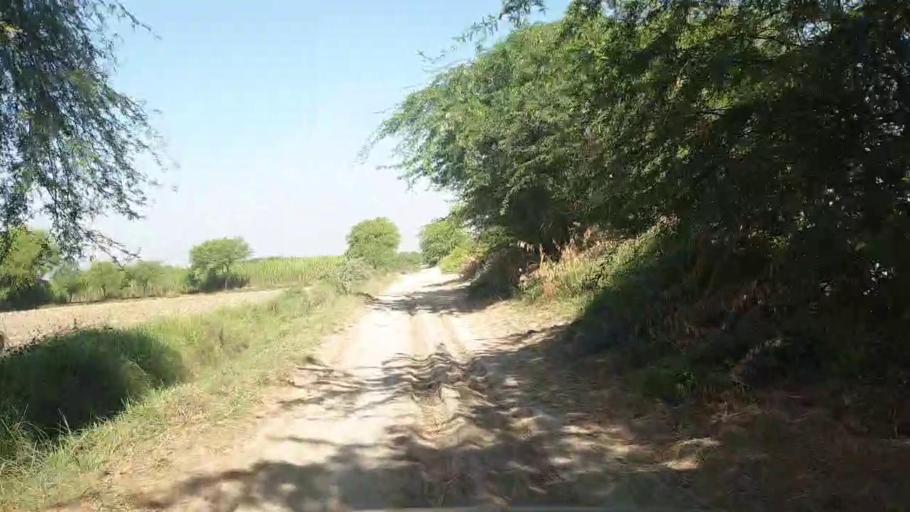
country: PK
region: Sindh
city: Talhar
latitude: 24.8194
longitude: 68.7836
